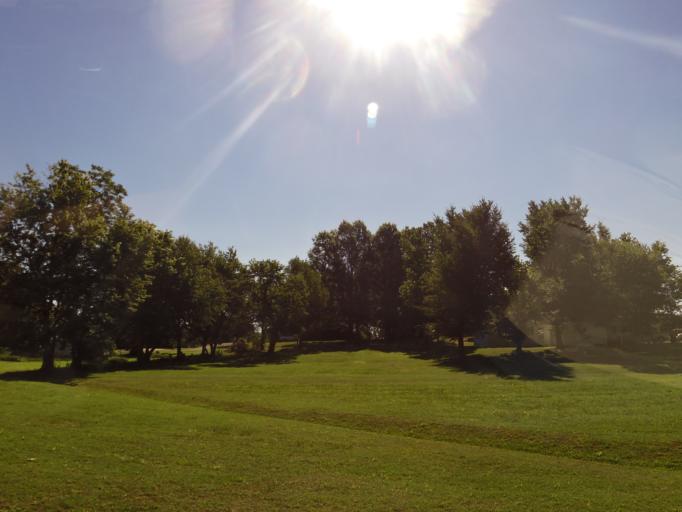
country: US
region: Arkansas
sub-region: Clay County
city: Piggott
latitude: 36.4279
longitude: -90.2714
